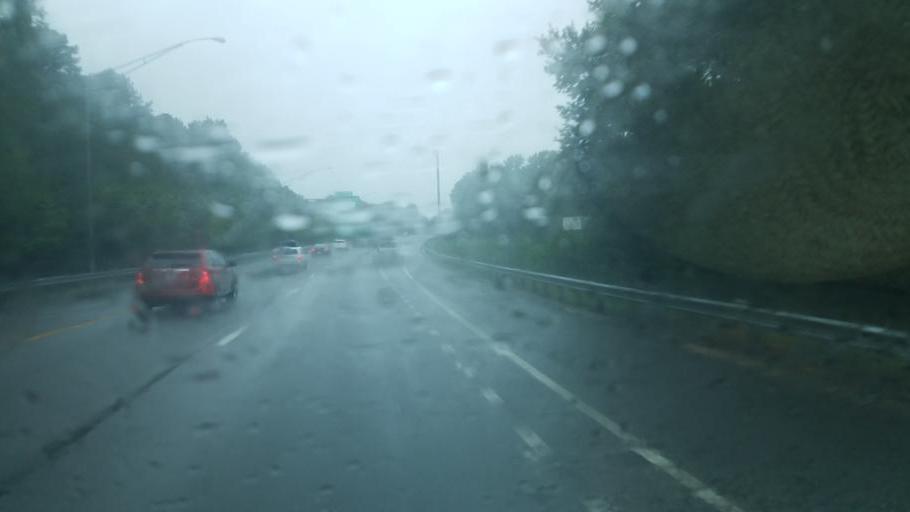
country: US
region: Virginia
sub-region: City of Portsmouth
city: Portsmouth Heights
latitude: 36.7805
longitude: -76.3911
